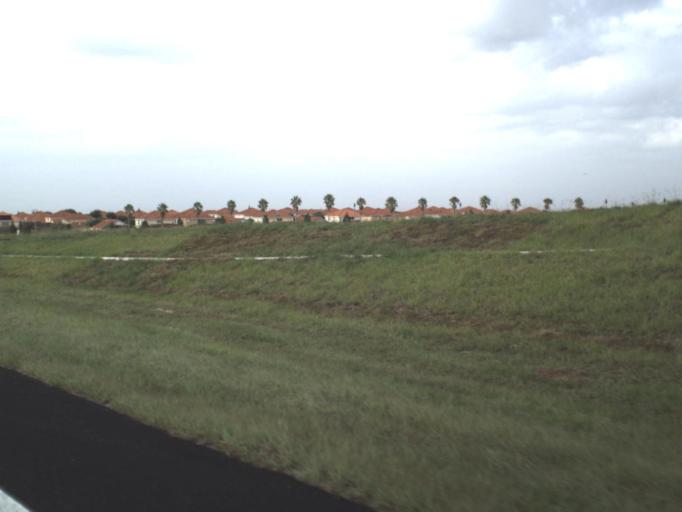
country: US
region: Florida
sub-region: Lake County
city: Four Corners
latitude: 28.2820
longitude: -81.6629
